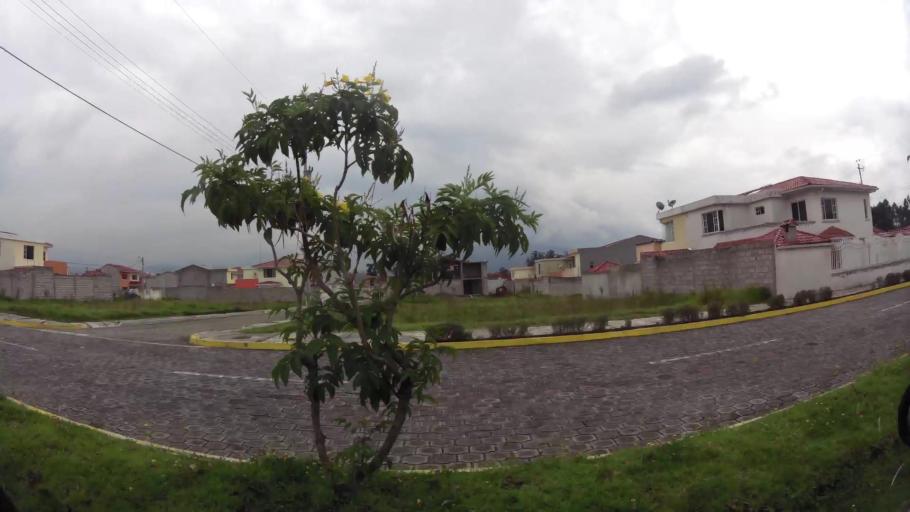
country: EC
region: Pichincha
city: Sangolqui
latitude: -0.3349
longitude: -78.4626
